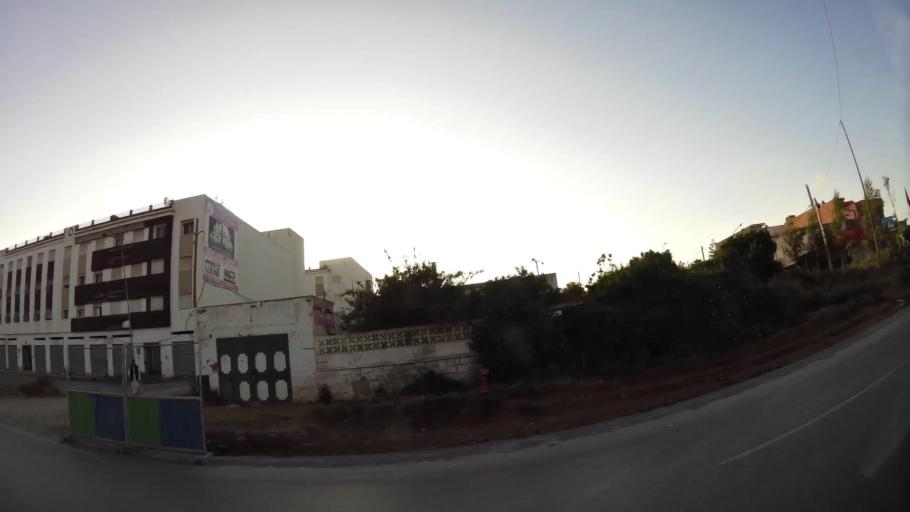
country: MA
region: Rabat-Sale-Zemmour-Zaer
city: Sale
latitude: 34.1267
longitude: -6.7362
